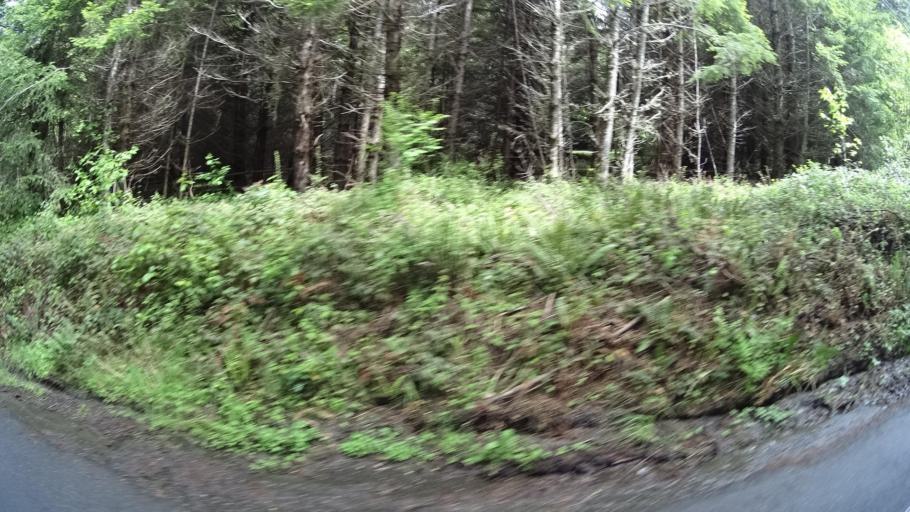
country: US
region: California
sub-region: Humboldt County
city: Bayside
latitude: 40.8344
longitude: -124.0179
